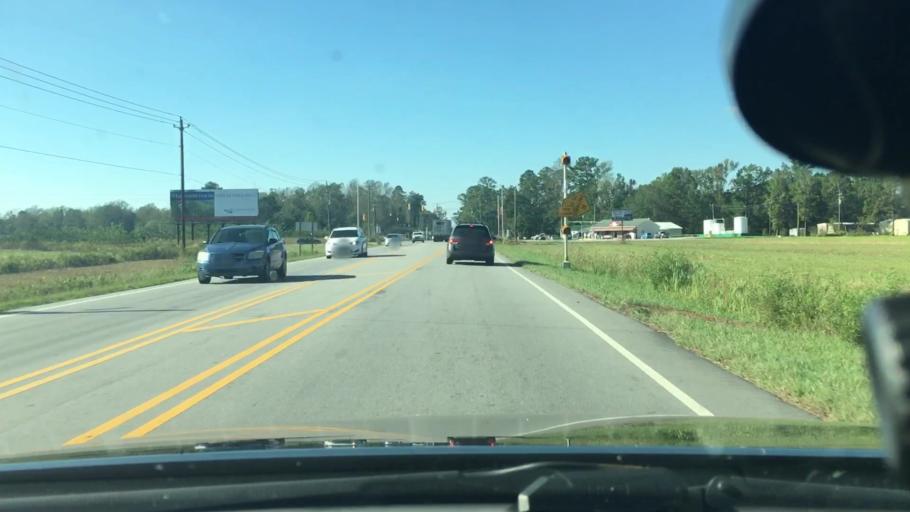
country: US
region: North Carolina
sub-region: Craven County
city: Vanceboro
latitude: 35.2486
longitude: -77.0876
